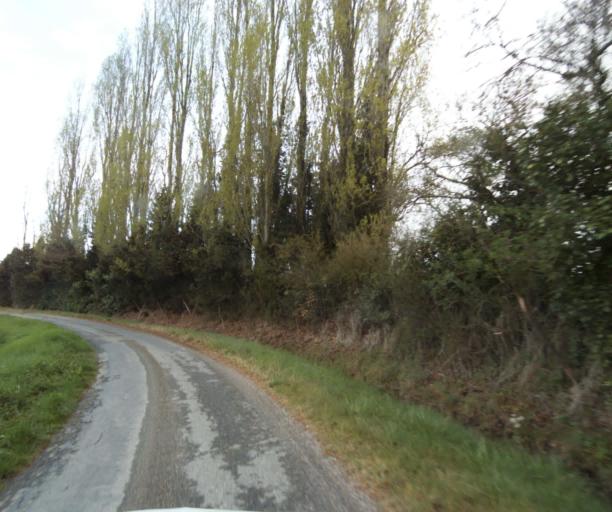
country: FR
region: Midi-Pyrenees
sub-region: Departement de l'Ariege
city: Saverdun
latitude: 43.2271
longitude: 1.5948
